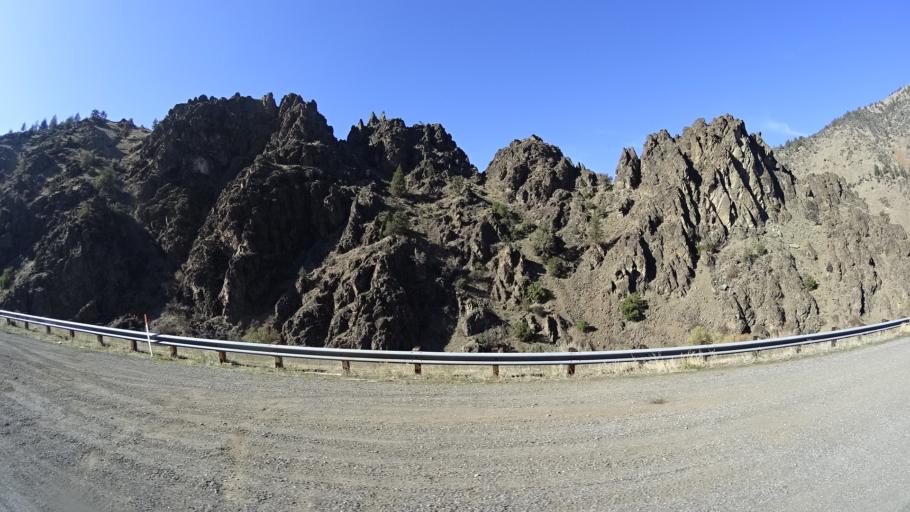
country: US
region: California
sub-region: Siskiyou County
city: Yreka
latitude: 41.8286
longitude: -122.5933
